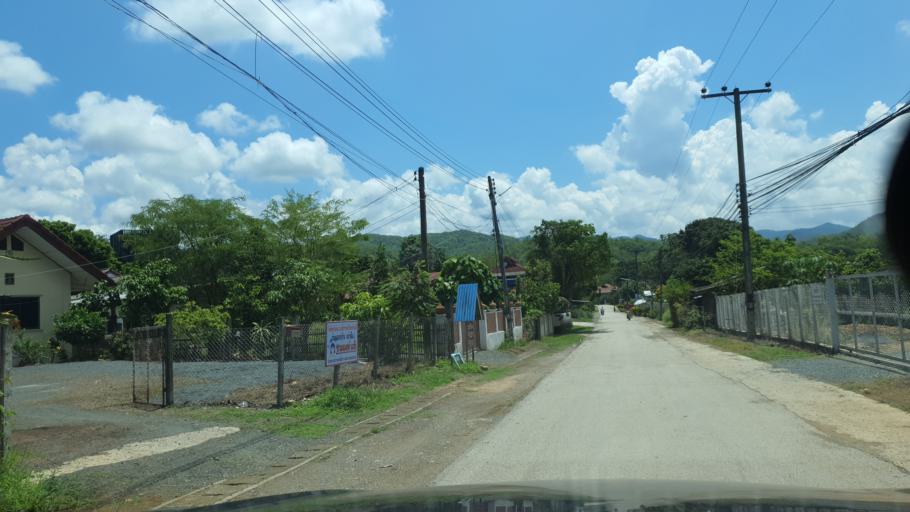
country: TH
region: Chiang Mai
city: Mae On
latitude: 18.8136
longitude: 99.2565
